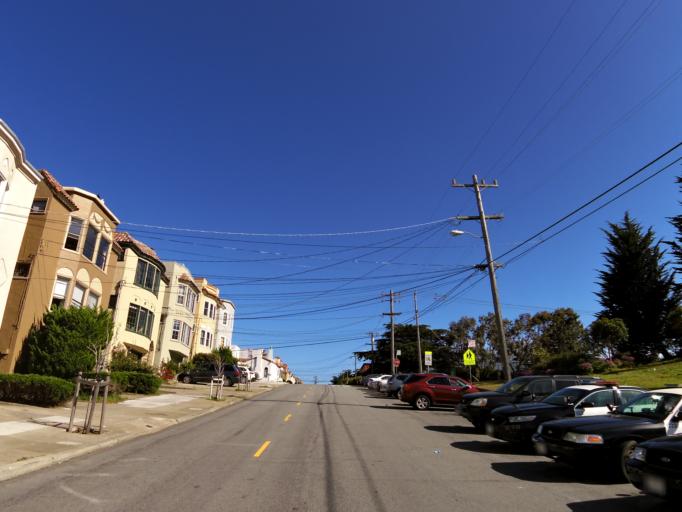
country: US
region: California
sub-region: San Mateo County
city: Daly City
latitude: 37.7441
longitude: -122.4812
